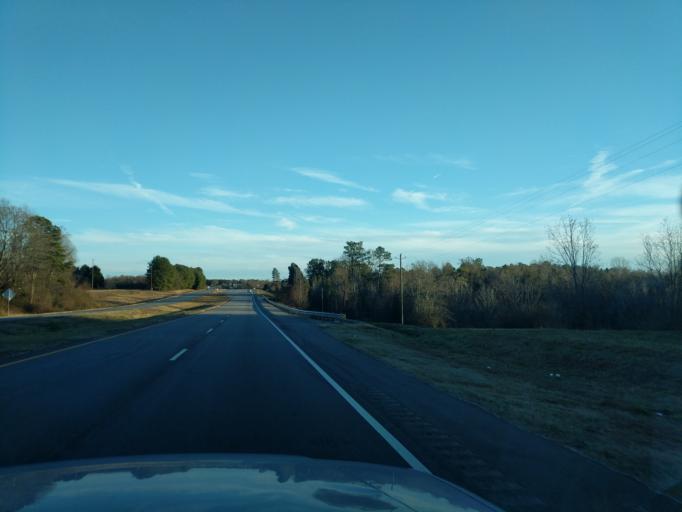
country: US
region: Georgia
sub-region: Franklin County
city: Lavonia
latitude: 34.4674
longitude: -83.1731
